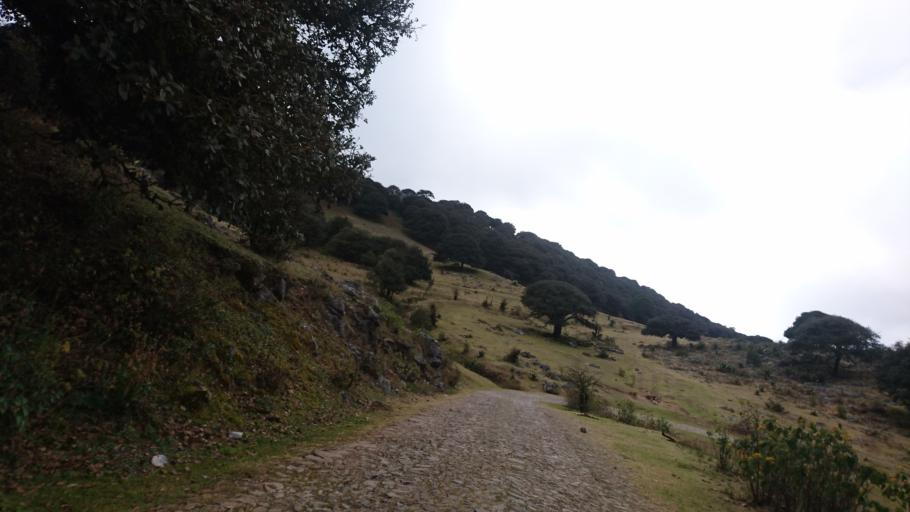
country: MX
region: San Luis Potosi
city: Zaragoza
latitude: 22.0689
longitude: -100.6415
